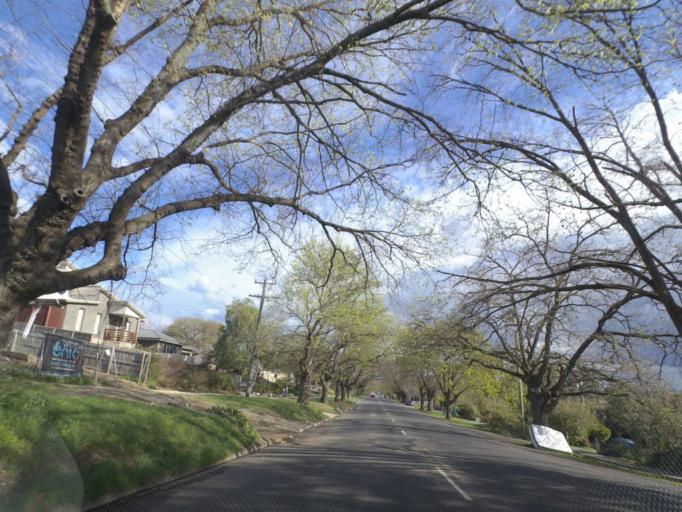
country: AU
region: Victoria
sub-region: Yarra Ranges
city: Lilydale
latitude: -37.7541
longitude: 145.3557
